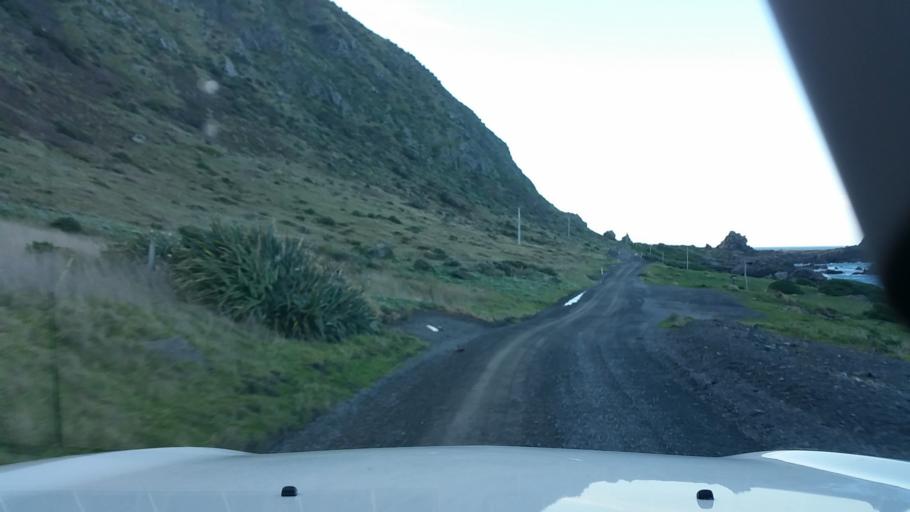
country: NZ
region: Wellington
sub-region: South Wairarapa District
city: Waipawa
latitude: -41.6058
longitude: 175.2671
